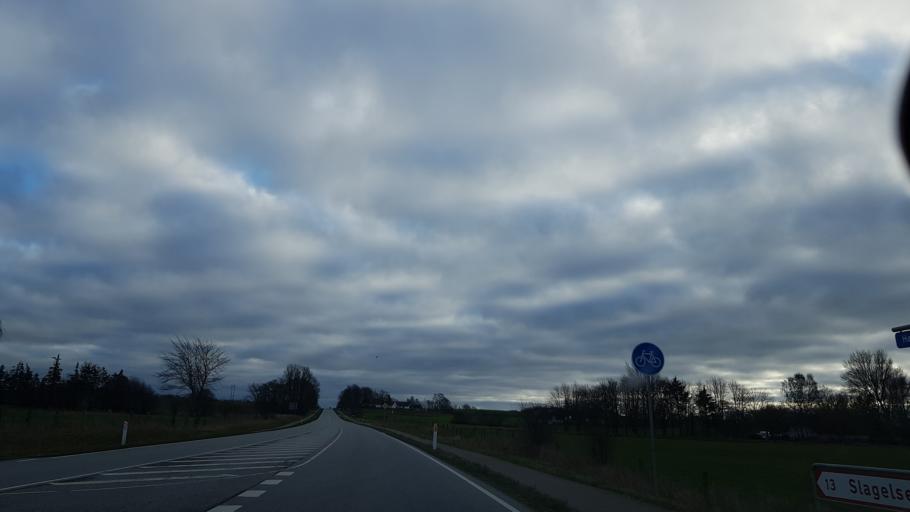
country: DK
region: Zealand
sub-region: Kalundborg Kommune
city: Hong
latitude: 55.5022
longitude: 11.2677
